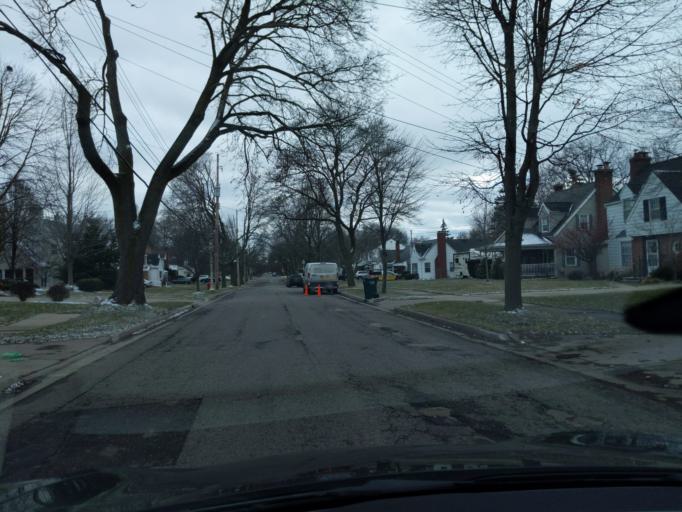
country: US
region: Michigan
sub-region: Ingham County
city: East Lansing
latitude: 42.7425
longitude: -84.5176
